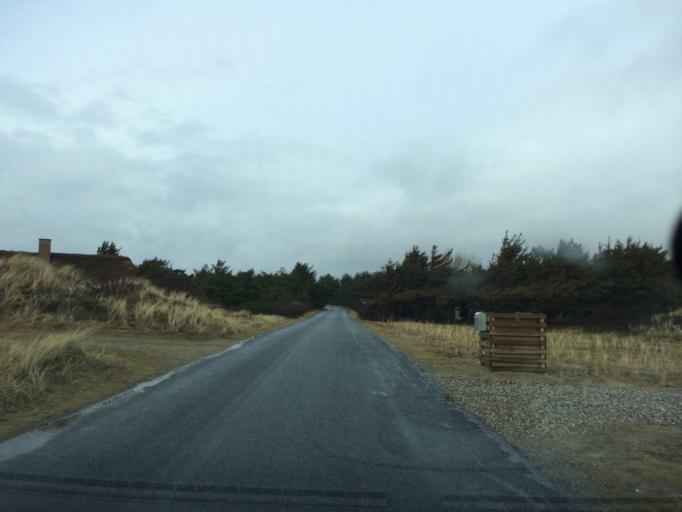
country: DK
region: Central Jutland
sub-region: Holstebro Kommune
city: Ulfborg
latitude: 56.2521
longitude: 8.1360
